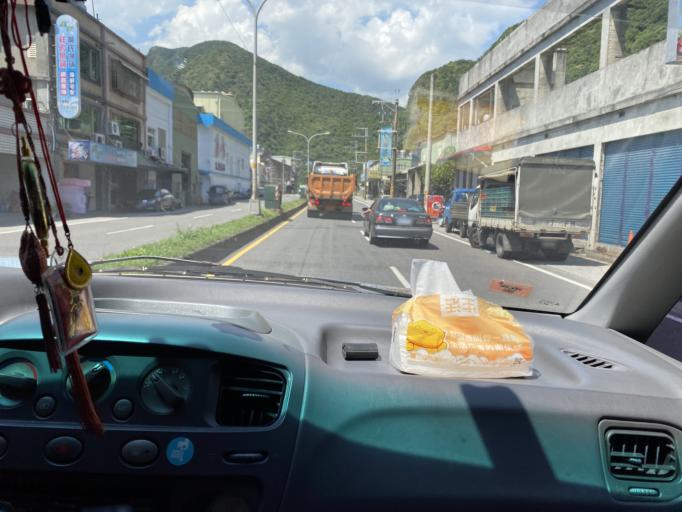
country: TW
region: Taiwan
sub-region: Yilan
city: Yilan
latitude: 24.9416
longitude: 121.8995
